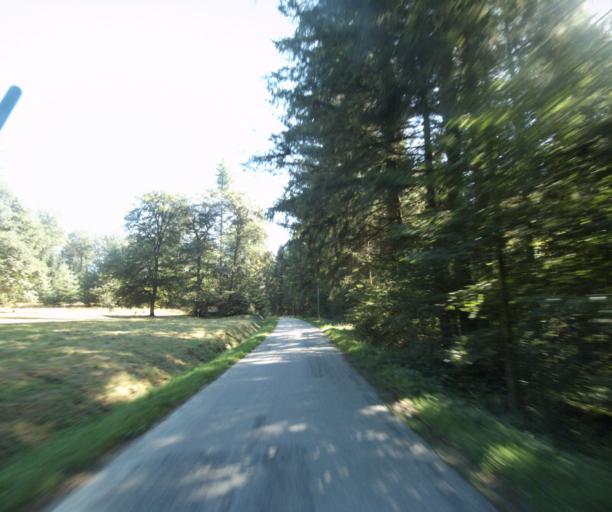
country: FR
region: Lorraine
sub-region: Departement des Vosges
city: Deyvillers
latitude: 48.1617
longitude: 6.5248
